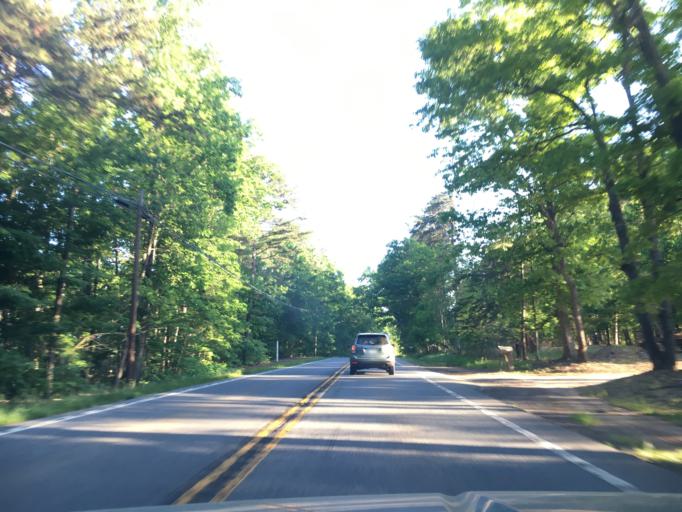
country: US
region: Virginia
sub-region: Campbell County
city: Rustburg
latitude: 37.2571
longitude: -79.1219
